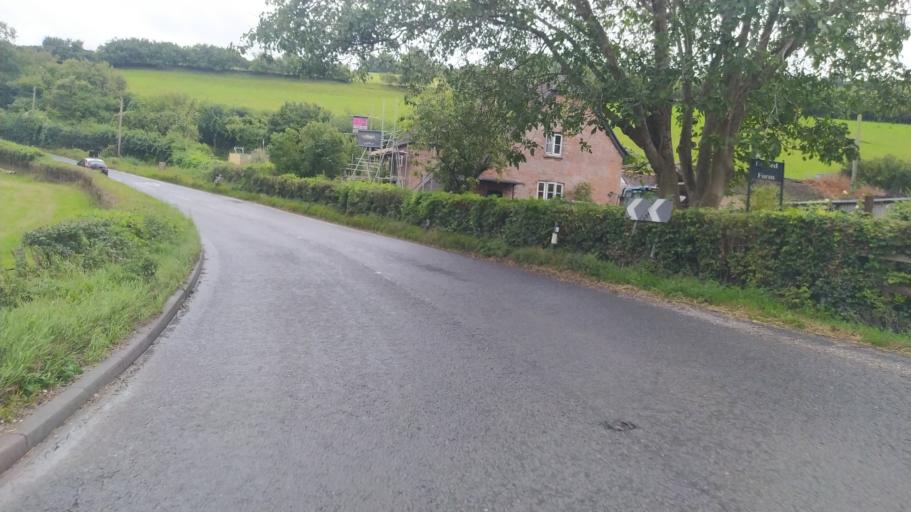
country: GB
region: England
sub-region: Dorset
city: Blandford Forum
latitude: 50.8840
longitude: -2.2165
